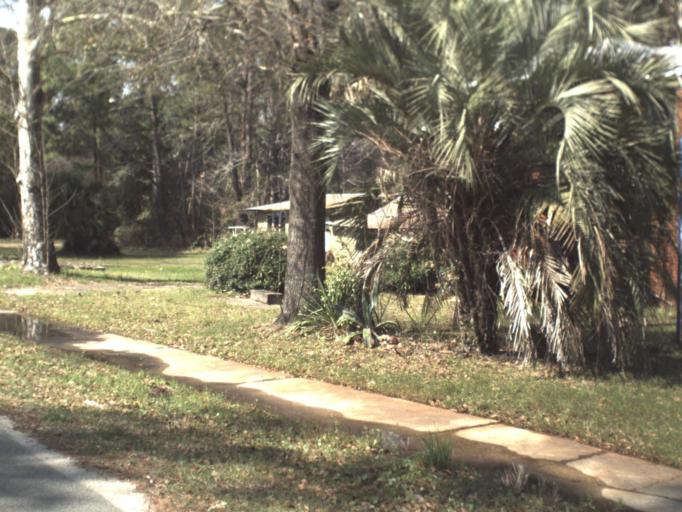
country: US
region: Florida
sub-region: Bay County
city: Lynn Haven
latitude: 30.2377
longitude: -85.6512
